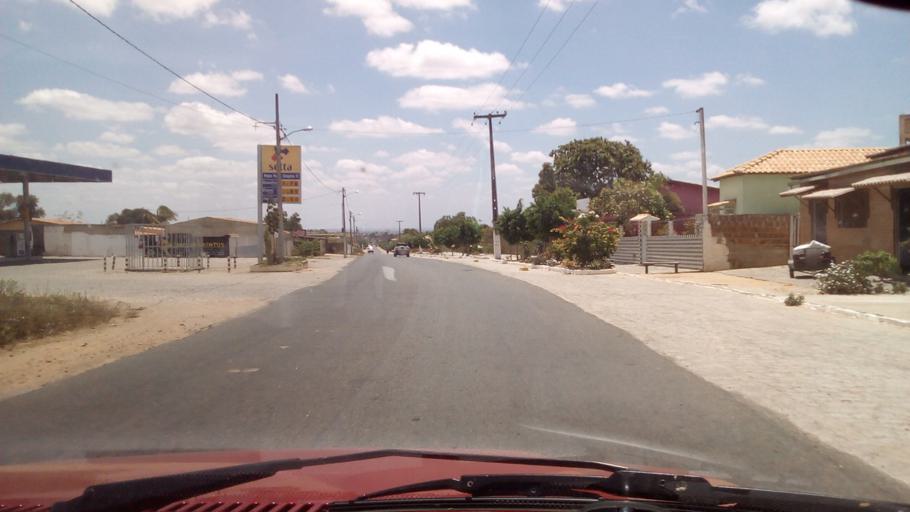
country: BR
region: Paraiba
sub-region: Cacimba De Dentro
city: Cacimba de Dentro
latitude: -6.6282
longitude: -35.7988
